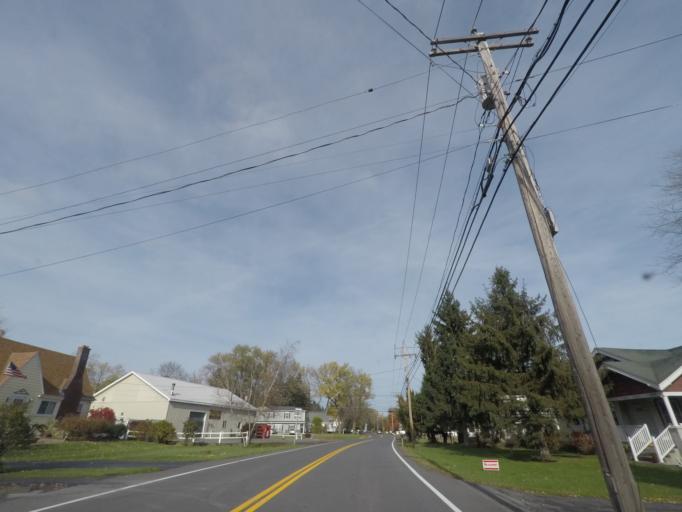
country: US
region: New York
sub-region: Schenectady County
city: Rotterdam
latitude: 42.7625
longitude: -73.9866
